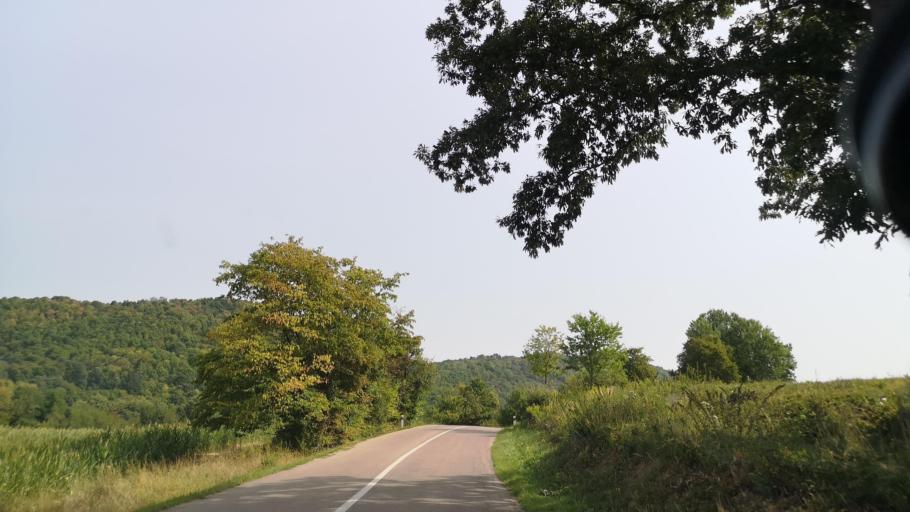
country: SK
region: Banskobystricky
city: Revuca
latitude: 48.6119
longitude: 20.1990
